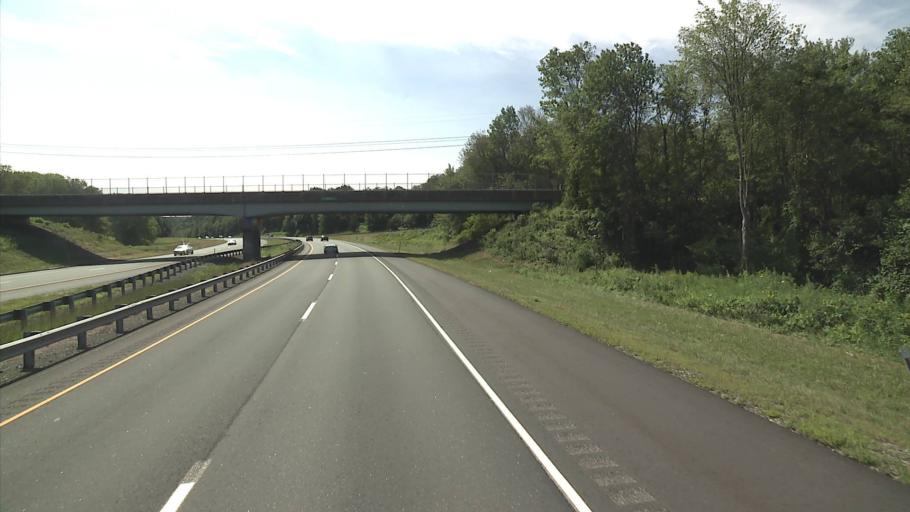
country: US
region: Connecticut
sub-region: Hartford County
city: Terramuggus
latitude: 41.6105
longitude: -72.4334
